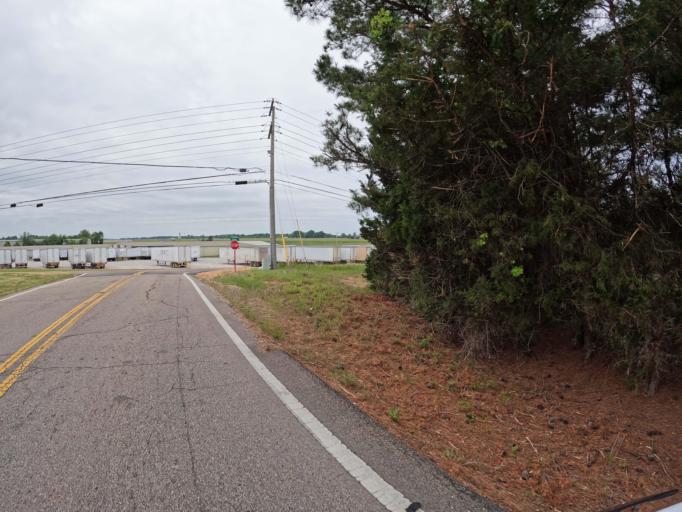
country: US
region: Mississippi
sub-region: Lee County
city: Tupelo
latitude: 34.2819
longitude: -88.7653
